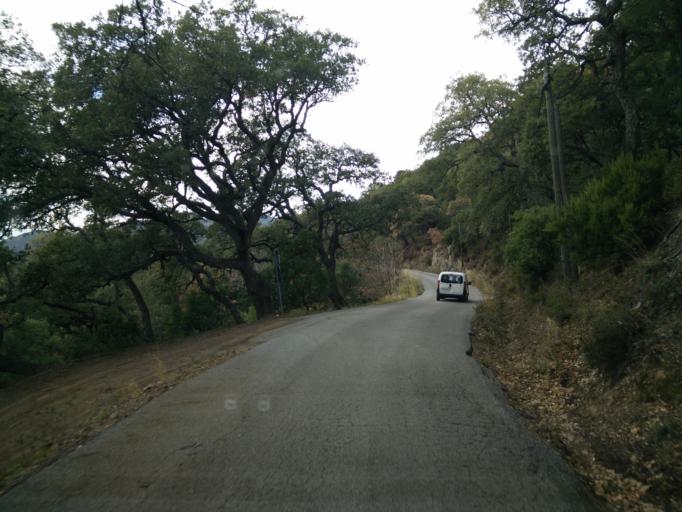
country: FR
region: Provence-Alpes-Cote d'Azur
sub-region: Departement du Var
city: Le Plan-de-la-Tour
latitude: 43.3665
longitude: 6.6048
